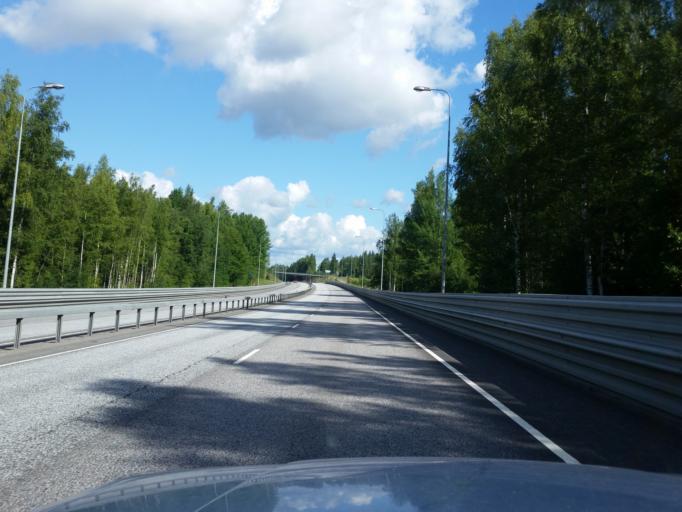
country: FI
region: Uusimaa
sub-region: Helsinki
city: Vihti
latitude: 60.3106
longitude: 24.3494
